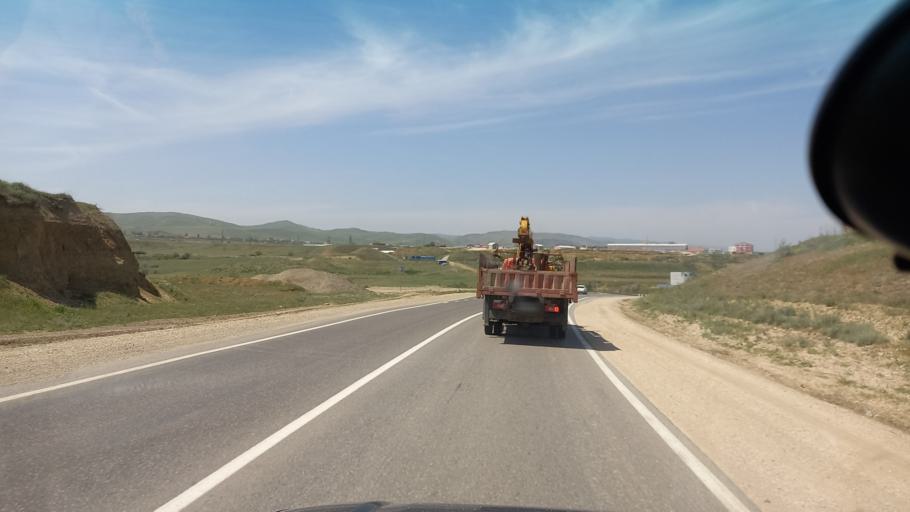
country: RU
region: Dagestan
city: Manas
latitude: 42.7108
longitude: 47.6744
